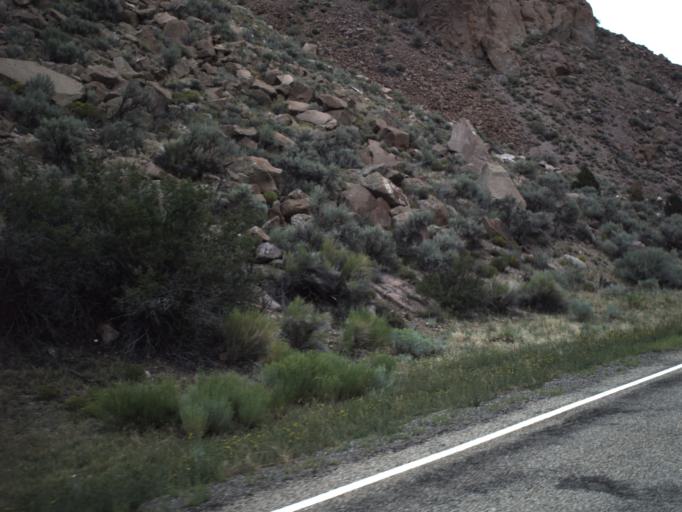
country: US
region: Utah
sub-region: Piute County
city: Junction
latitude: 38.1924
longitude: -112.1315
